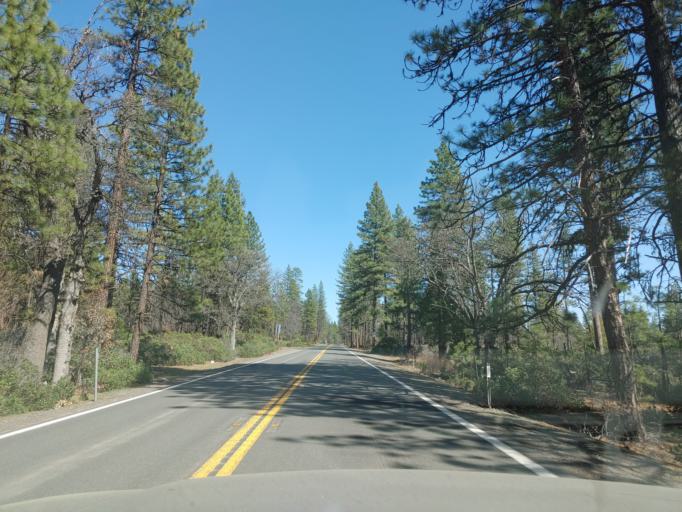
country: US
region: California
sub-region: Shasta County
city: Burney
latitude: 41.0084
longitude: -121.6438
